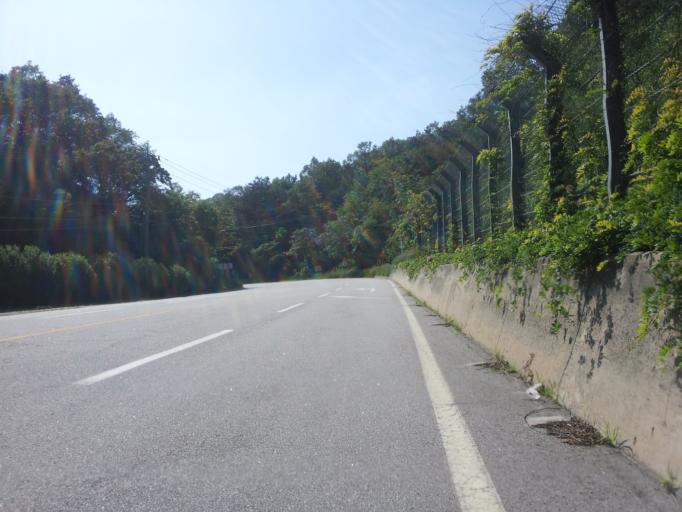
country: KR
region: Chungcheongbuk-do
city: Okcheon
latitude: 36.4785
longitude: 127.6439
